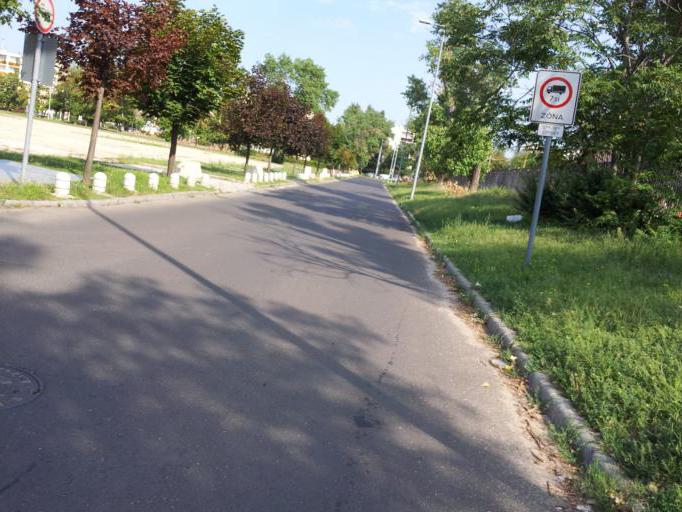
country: HU
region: Budapest
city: Budapest IX. keruelet
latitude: 47.4731
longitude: 19.0837
